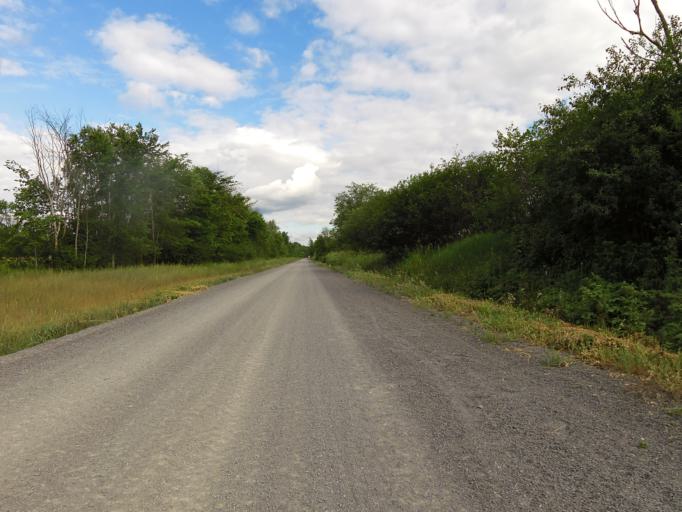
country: CA
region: Ontario
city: Arnprior
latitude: 45.3060
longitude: -76.2727
